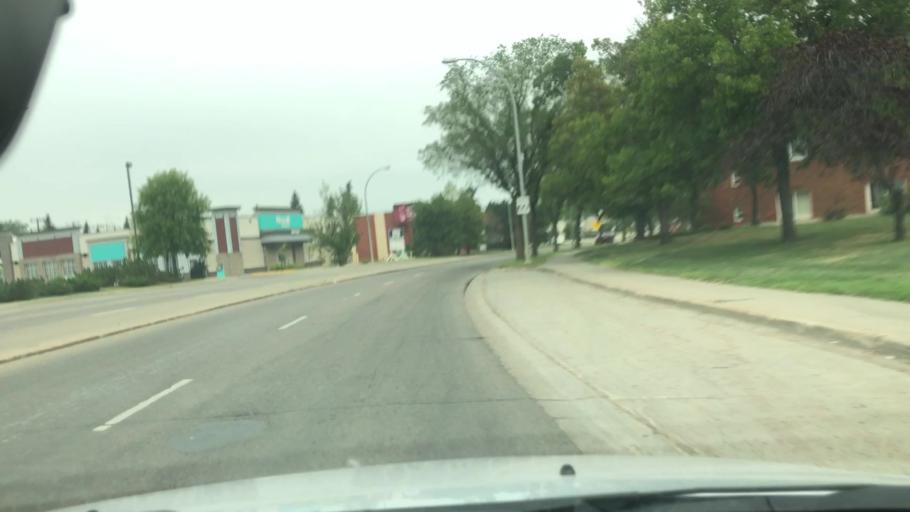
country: CA
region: Alberta
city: Edmonton
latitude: 53.5635
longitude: -113.5514
